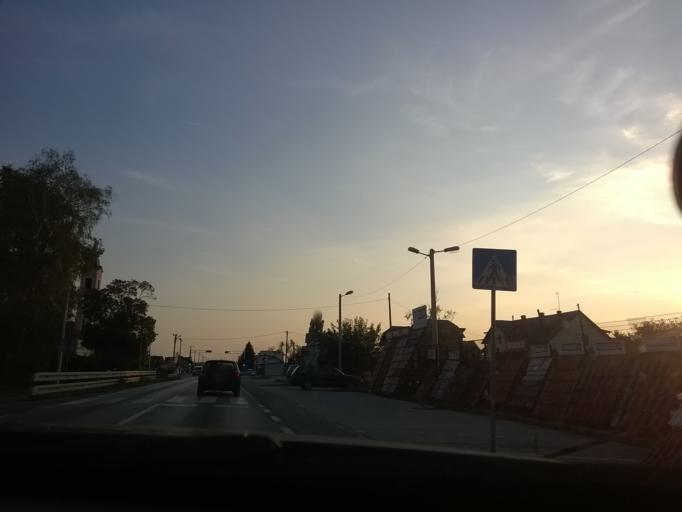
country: HR
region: Grad Zagreb
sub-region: Sesvete
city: Sesvete
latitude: 45.8647
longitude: 16.1545
